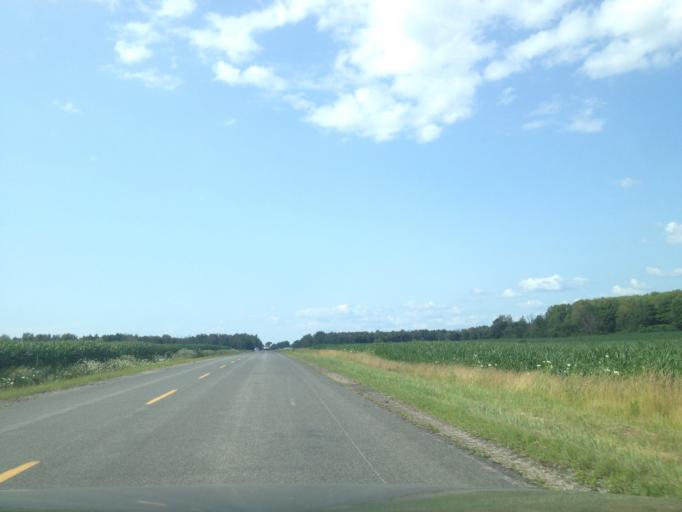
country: CA
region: Ontario
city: Aylmer
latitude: 42.6775
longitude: -80.8598
